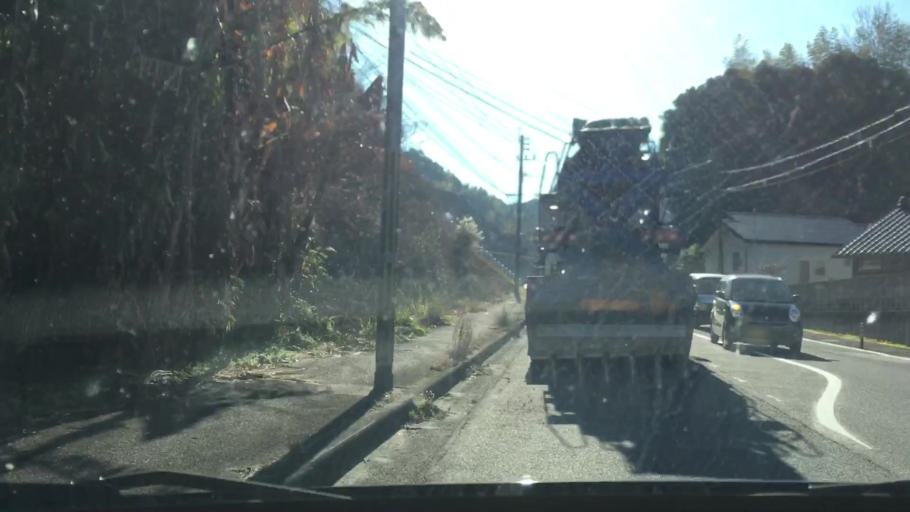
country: JP
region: Kagoshima
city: Kajiki
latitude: 31.7557
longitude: 130.6777
